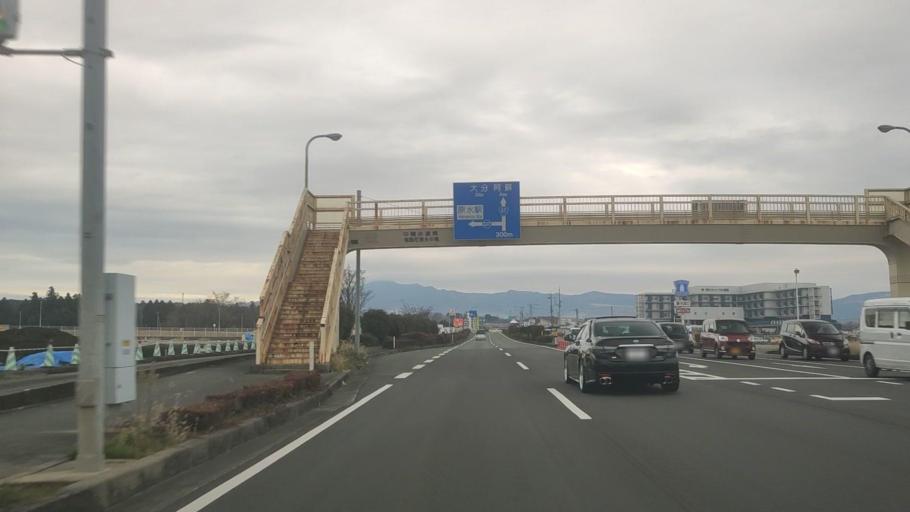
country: JP
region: Kumamoto
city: Ozu
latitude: 32.8718
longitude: 130.8450
